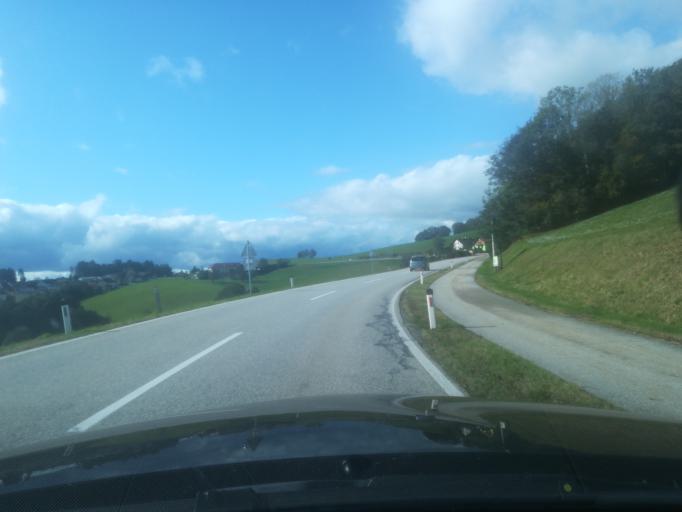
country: AT
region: Upper Austria
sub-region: Politischer Bezirk Urfahr-Umgebung
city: Eidenberg
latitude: 48.3617
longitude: 14.2521
